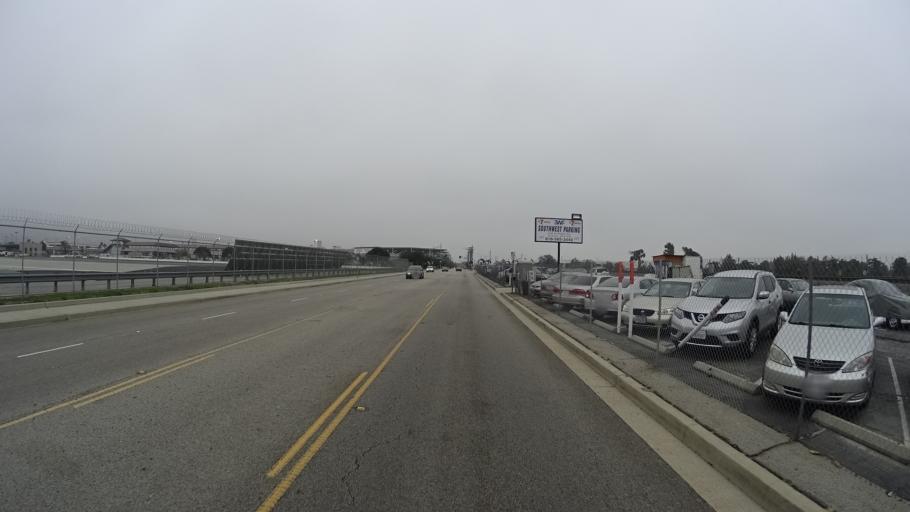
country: US
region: California
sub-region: Los Angeles County
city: North Hollywood
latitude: 34.1936
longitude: -118.3561
